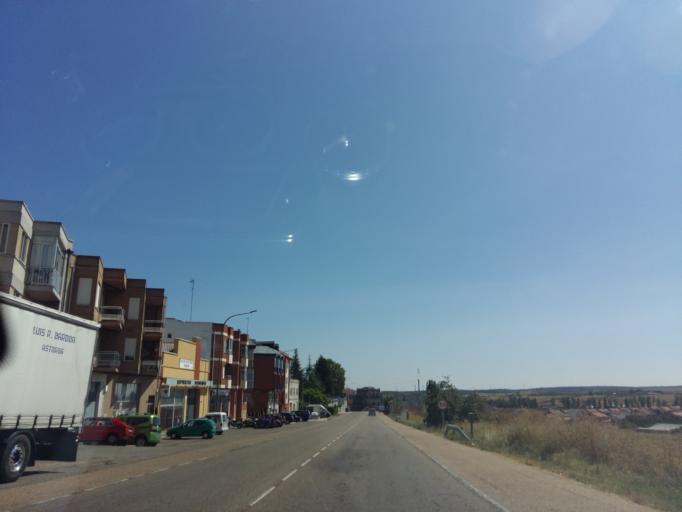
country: ES
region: Castille and Leon
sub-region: Provincia de Leon
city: Astorga
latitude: 42.4582
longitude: -6.0629
